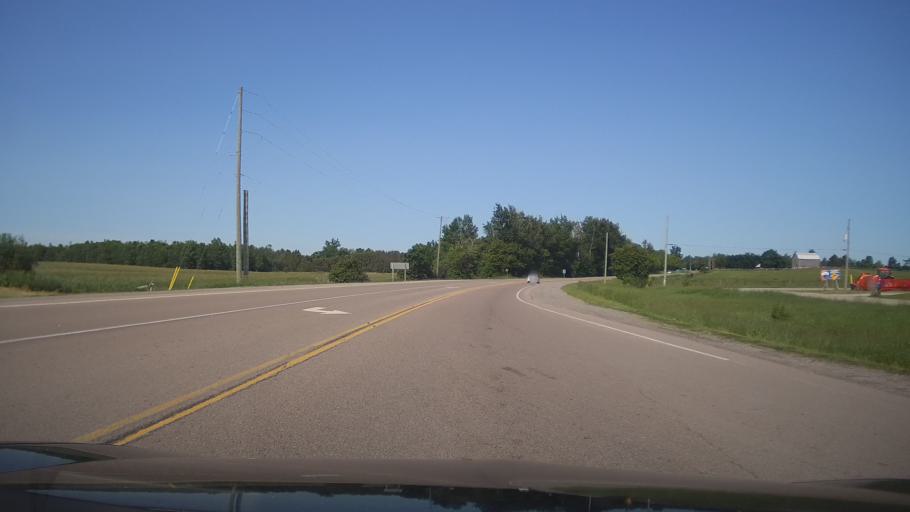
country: CA
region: Ontario
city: Omemee
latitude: 44.3475
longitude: -78.7954
